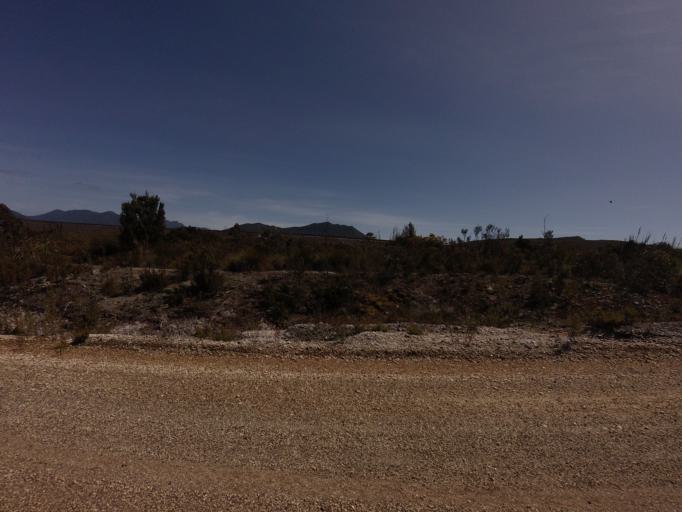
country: AU
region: Tasmania
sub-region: Huon Valley
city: Geeveston
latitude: -43.0320
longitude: 146.3033
